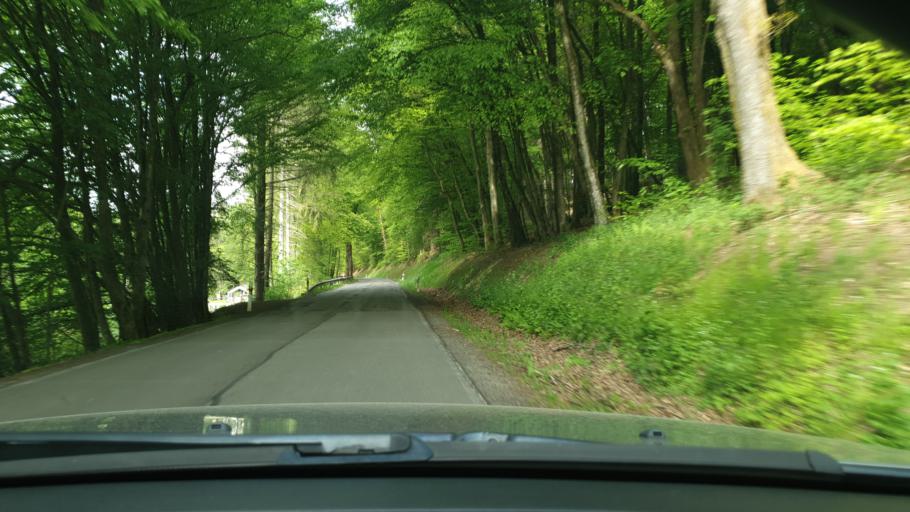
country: DE
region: Rheinland-Pfalz
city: Gerhardsbrunn
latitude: 49.3364
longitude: 7.5260
